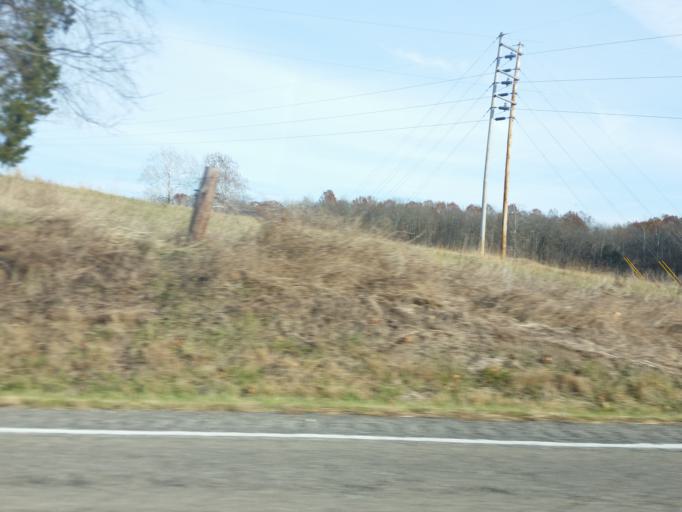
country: US
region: Kentucky
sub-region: Pendleton County
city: Falmouth
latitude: 38.6051
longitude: -84.3038
